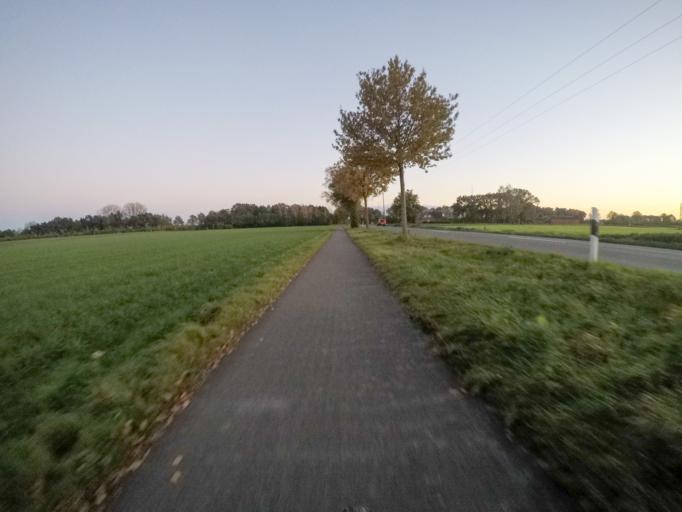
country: DE
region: North Rhine-Westphalia
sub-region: Regierungsbezirk Dusseldorf
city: Bocholt
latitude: 51.8052
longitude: 6.5737
